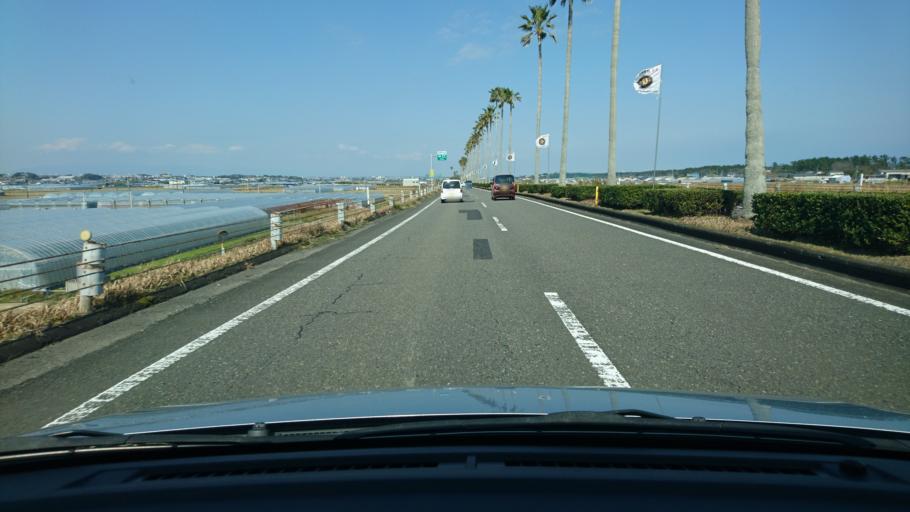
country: JP
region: Miyazaki
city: Miyazaki-shi
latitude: 31.8394
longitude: 131.4449
